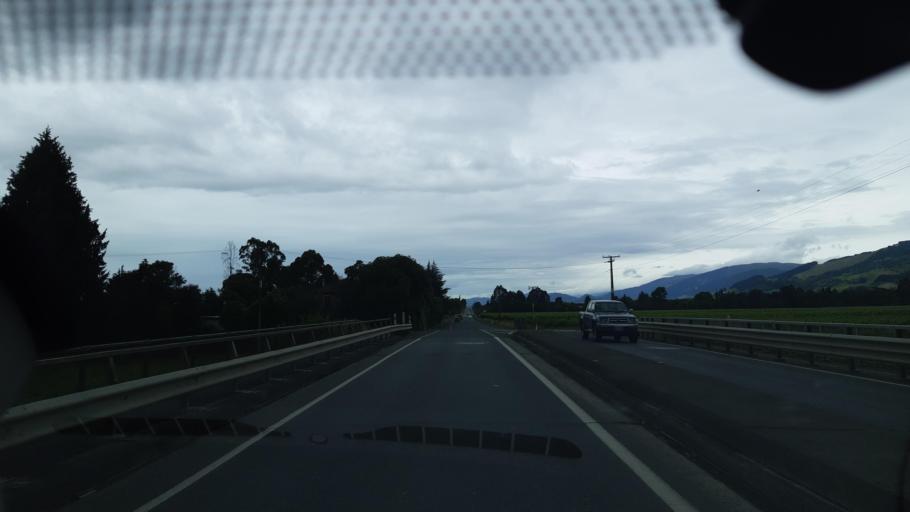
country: NZ
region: Tasman
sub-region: Tasman District
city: Brightwater
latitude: -41.3755
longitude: 173.1198
